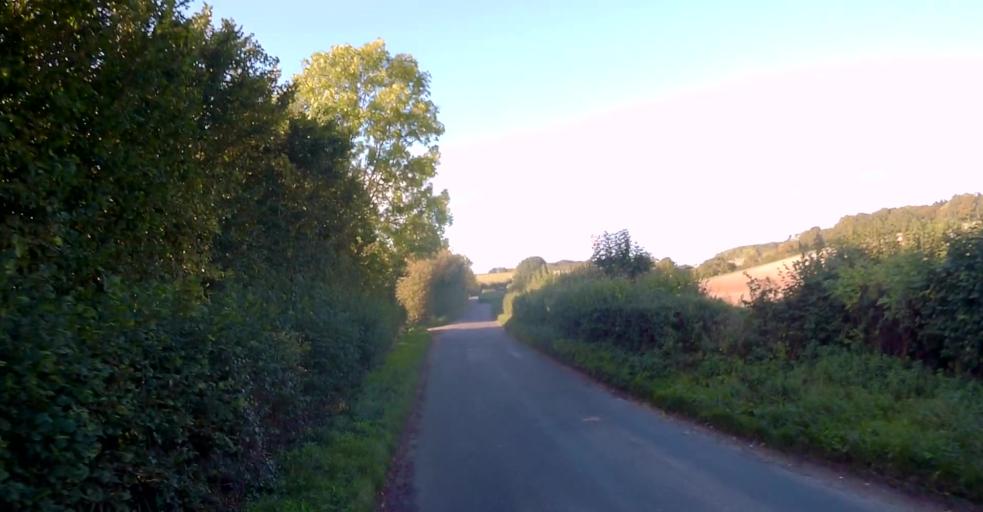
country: GB
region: England
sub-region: Hampshire
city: Long Sutton
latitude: 51.2292
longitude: -0.9254
